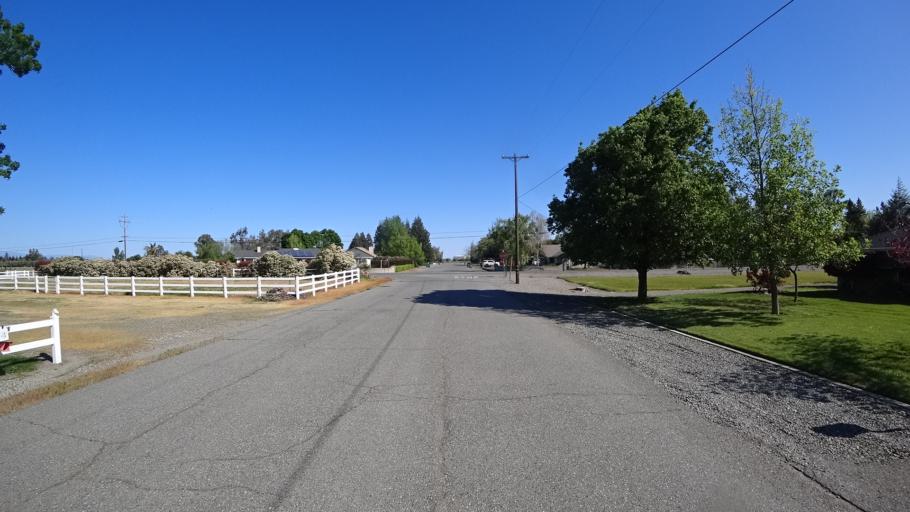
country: US
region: California
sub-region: Glenn County
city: Orland
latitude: 39.7285
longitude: -122.1654
